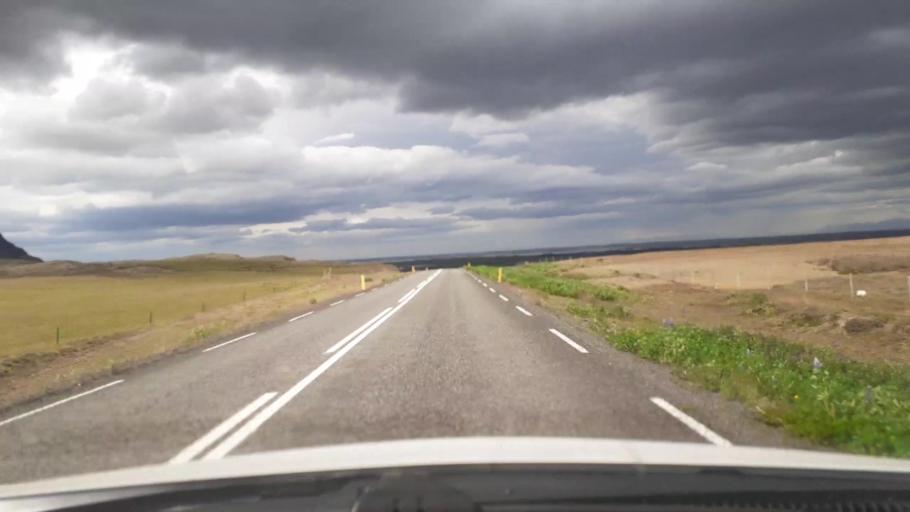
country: IS
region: West
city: Borgarnes
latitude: 64.5448
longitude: -21.6702
